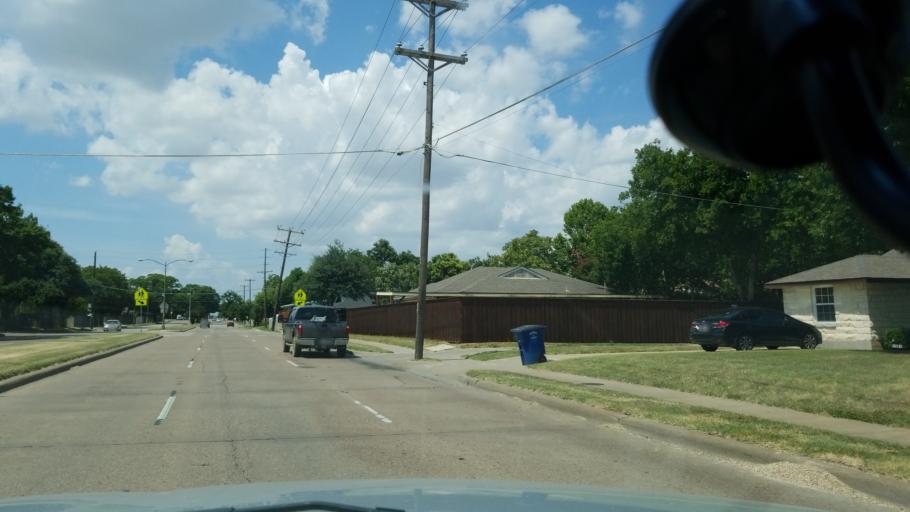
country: US
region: Texas
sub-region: Dallas County
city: Cockrell Hill
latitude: 32.7229
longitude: -96.8743
